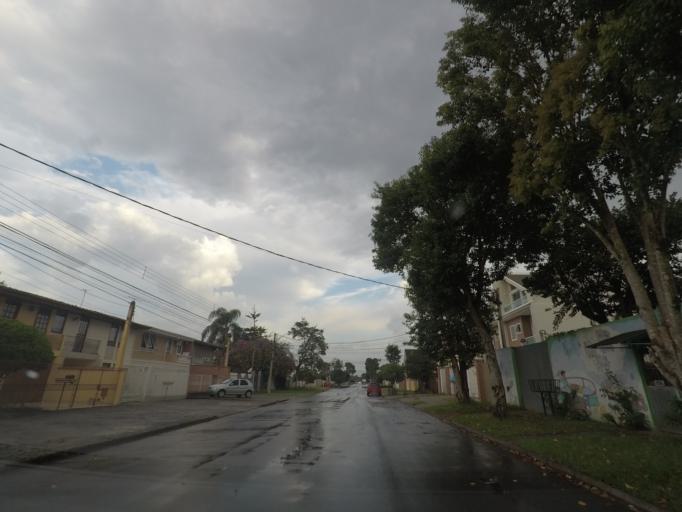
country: BR
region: Parana
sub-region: Sao Jose Dos Pinhais
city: Sao Jose dos Pinhais
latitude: -25.4867
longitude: -49.2502
